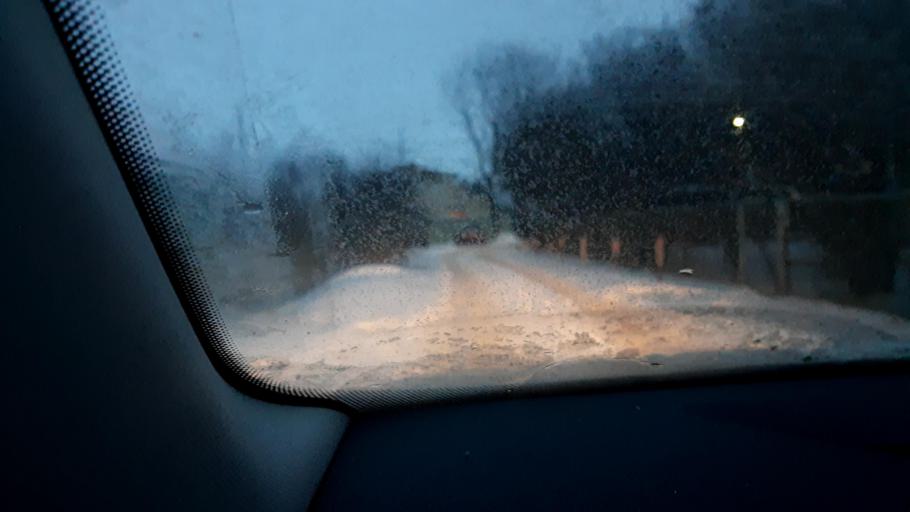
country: RU
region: Moskovskaya
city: Yam
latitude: 55.4843
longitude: 37.7182
